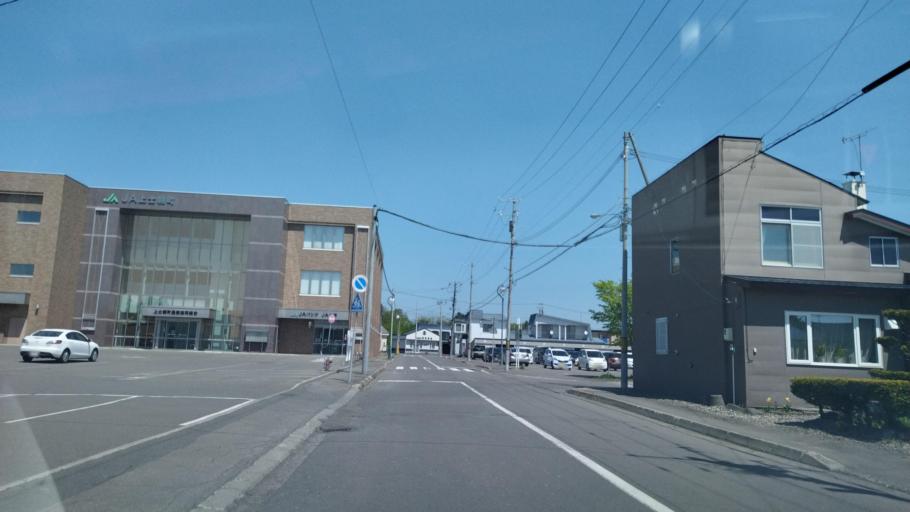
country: JP
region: Hokkaido
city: Otofuke
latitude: 43.2322
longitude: 143.2909
